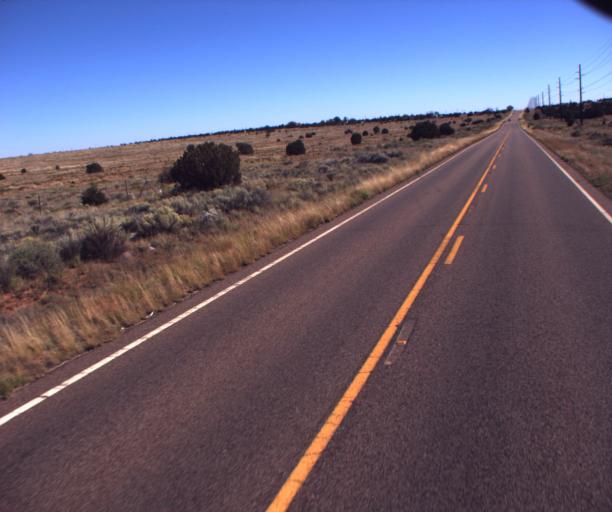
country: US
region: Arizona
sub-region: Navajo County
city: Taylor
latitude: 34.4835
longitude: -110.2644
